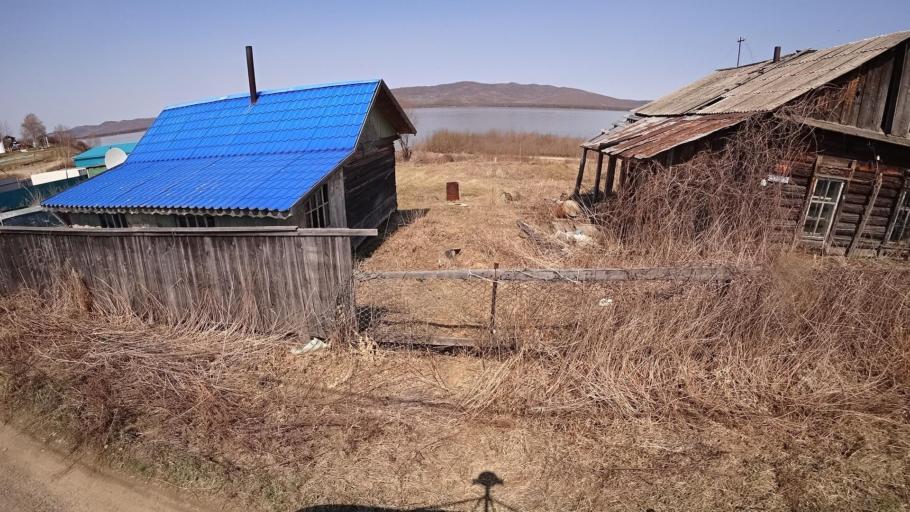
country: RU
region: Khabarovsk Krai
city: Selikhino
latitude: 50.6682
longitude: 137.4019
